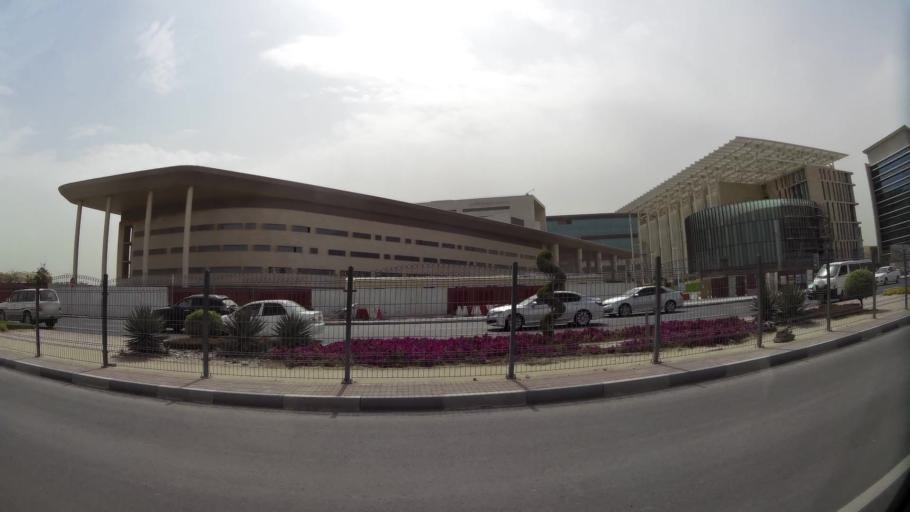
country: QA
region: Baladiyat ad Dawhah
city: Doha
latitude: 25.2960
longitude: 51.5107
